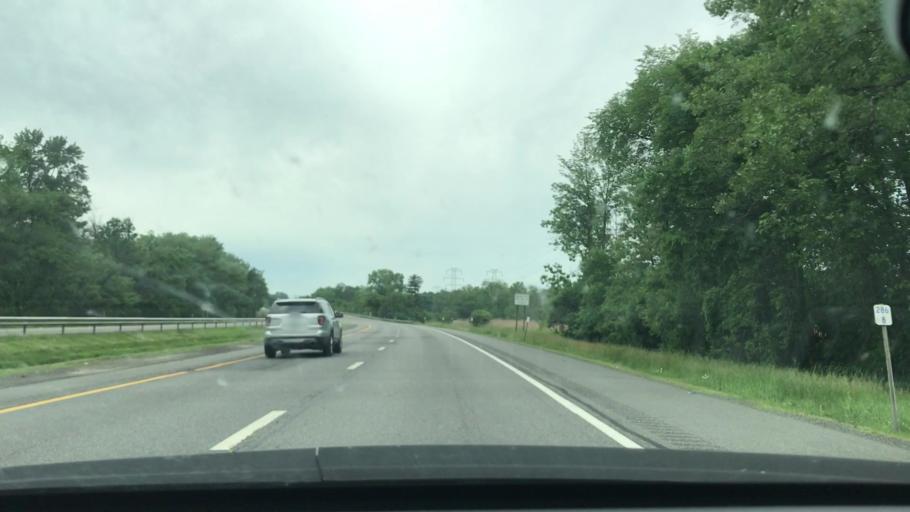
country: US
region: New York
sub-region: Onondaga County
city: Liverpool
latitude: 43.1182
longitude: -76.2351
